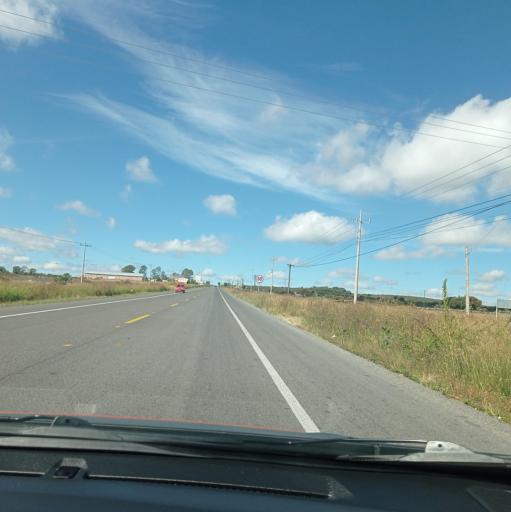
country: MX
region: Jalisco
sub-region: San Julian
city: Colonia Veintitres de Mayo
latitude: 21.0120
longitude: -102.2071
